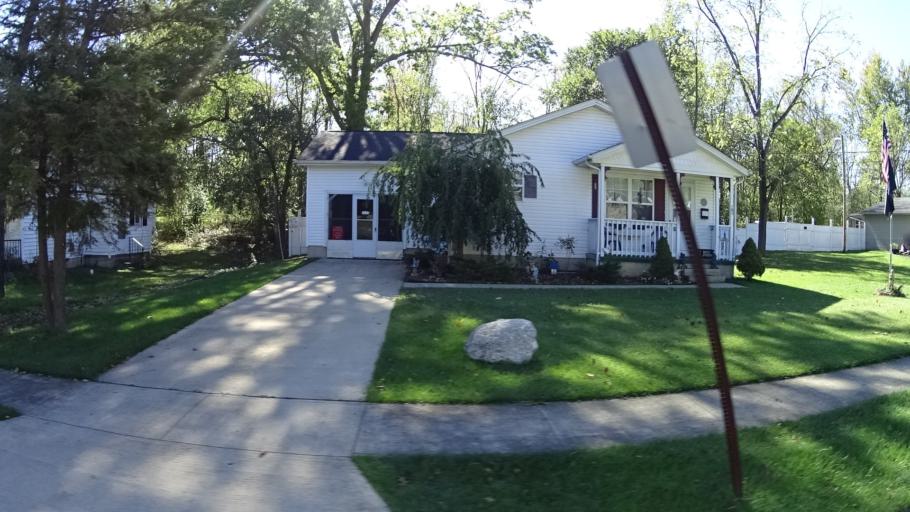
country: US
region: Ohio
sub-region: Lorain County
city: Oberlin
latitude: 41.2873
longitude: -82.2109
